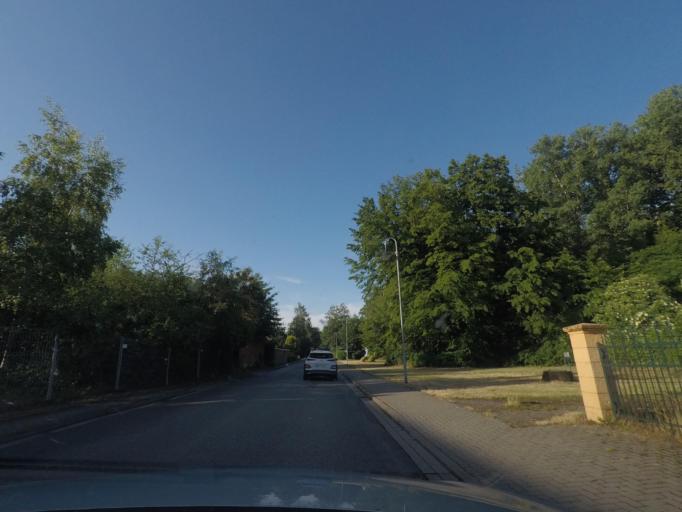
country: DE
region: Saxony-Anhalt
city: Huy-Neinstedt
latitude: 52.0136
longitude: 10.8982
